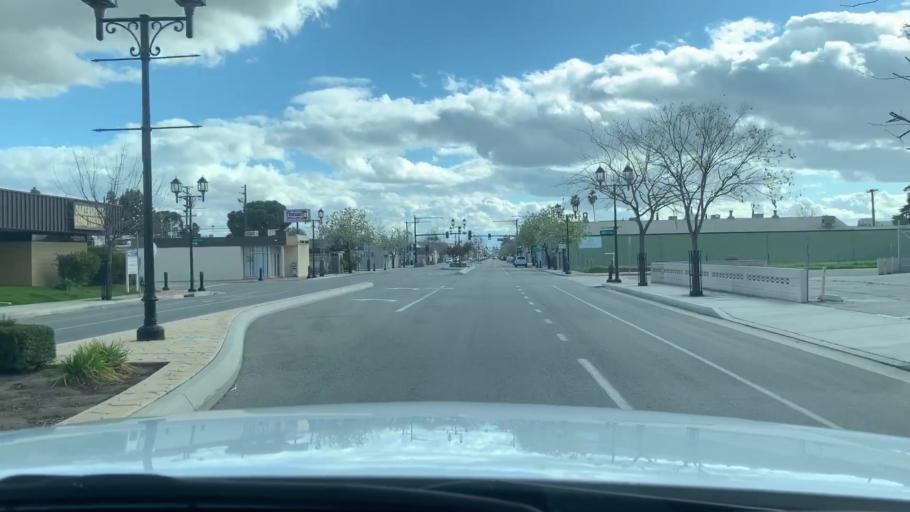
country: US
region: California
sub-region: Kern County
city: Bakersfield
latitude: 35.3795
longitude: -119.0106
